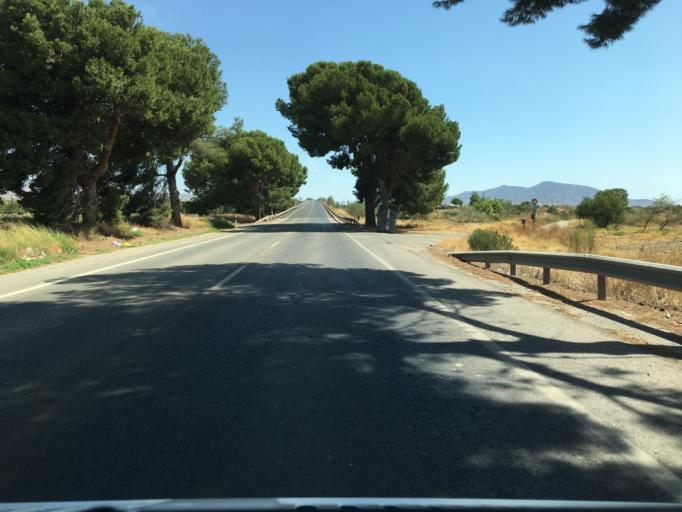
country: ES
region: Andalusia
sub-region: Provincia de Almeria
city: Huercal-Overa
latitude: 37.4240
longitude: -1.9182
